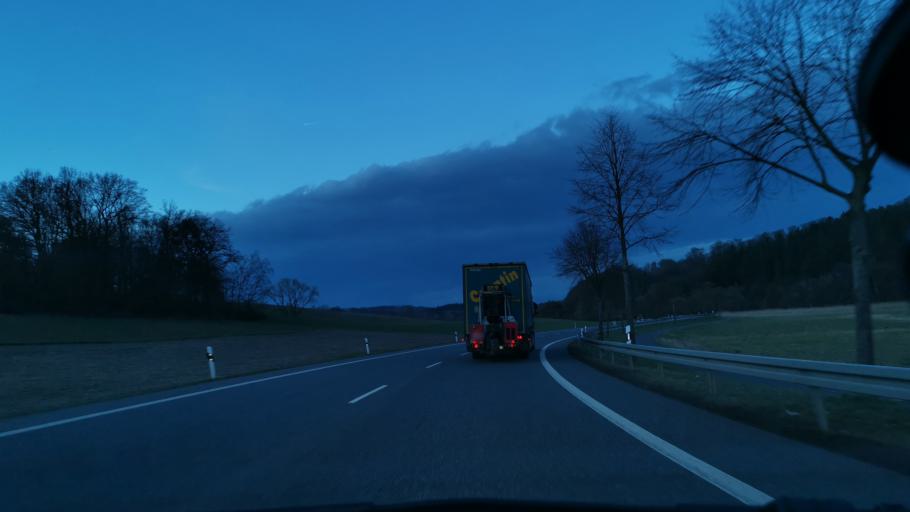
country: DE
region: Hesse
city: Bebra
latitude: 50.9981
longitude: 9.8118
